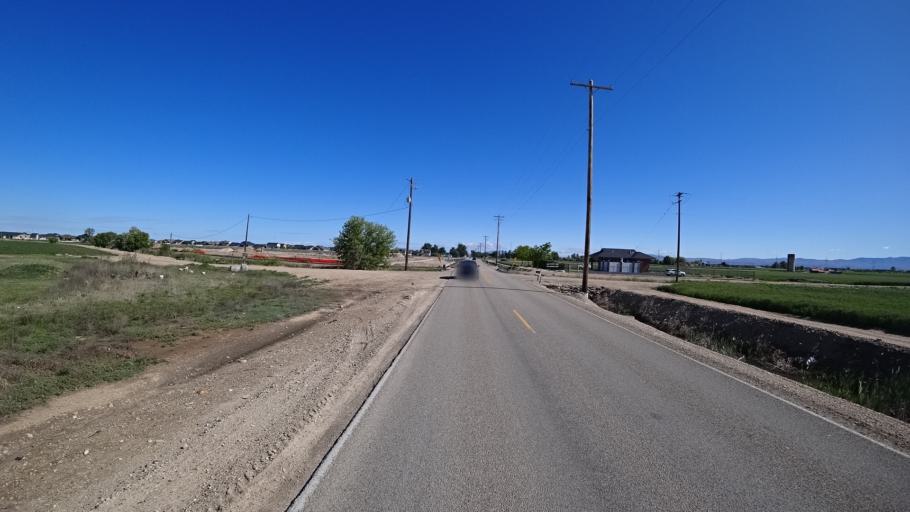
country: US
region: Idaho
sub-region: Ada County
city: Star
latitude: 43.6420
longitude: -116.4537
